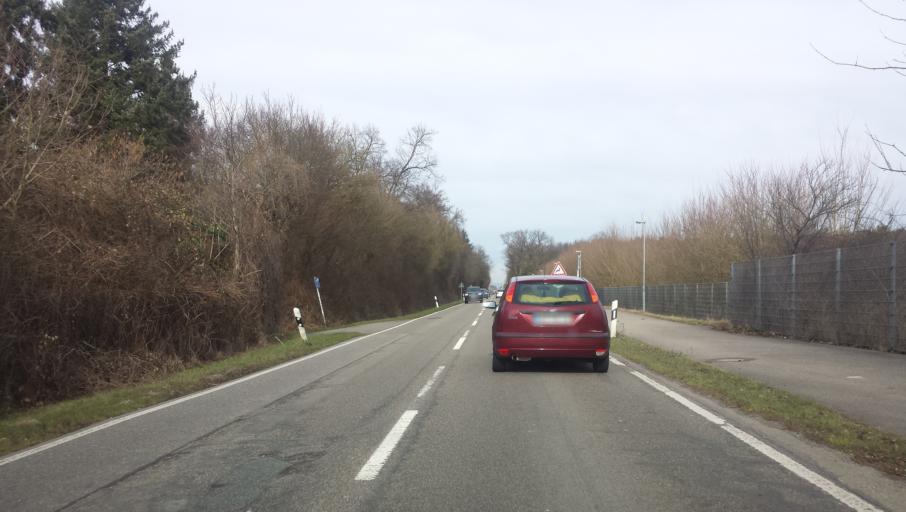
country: DE
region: Baden-Wuerttemberg
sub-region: Karlsruhe Region
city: Waghausel
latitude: 49.2273
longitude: 8.5297
